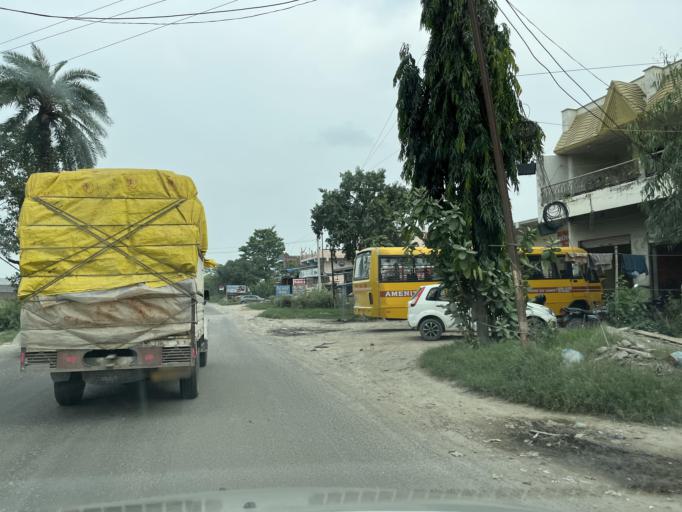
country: IN
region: Uttar Pradesh
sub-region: Rampur
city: Bilaspur
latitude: 29.0364
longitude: 79.2555
